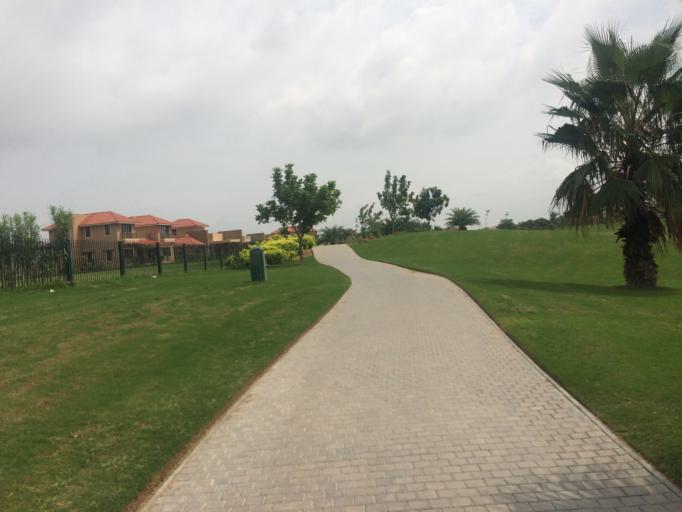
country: IN
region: Gujarat
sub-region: Ahmadabad
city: Sanand
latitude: 23.0191
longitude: 72.3586
